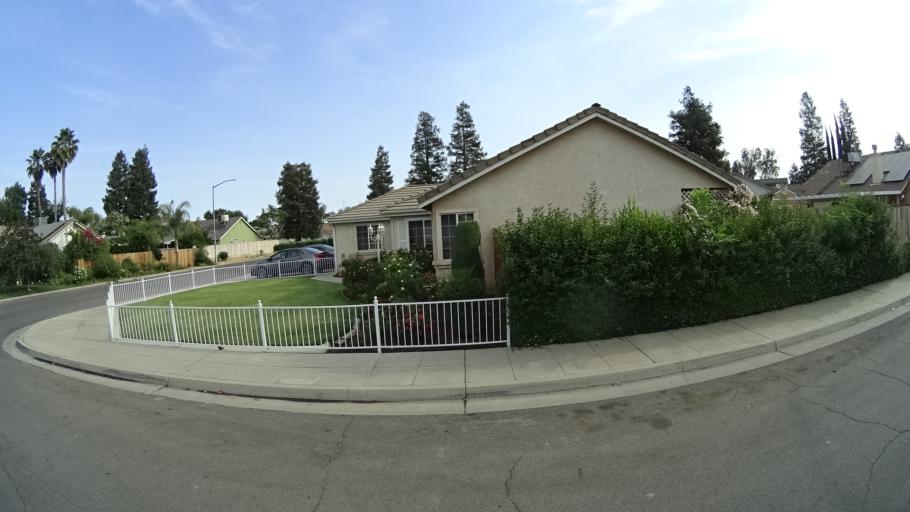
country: US
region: California
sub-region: Fresno County
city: West Park
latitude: 36.7730
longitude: -119.8636
